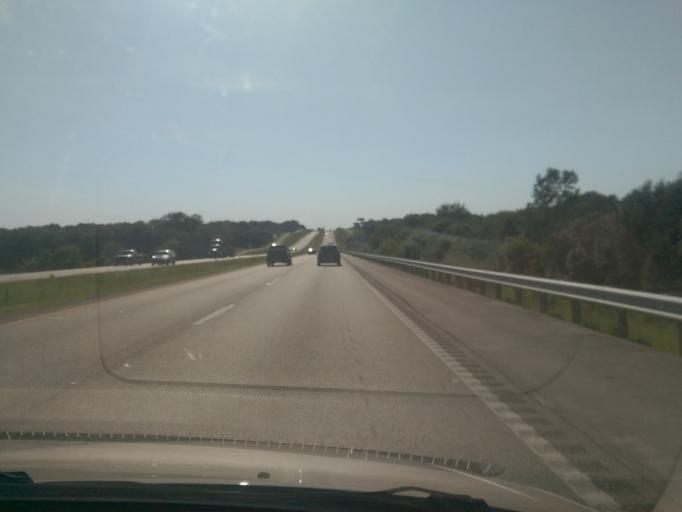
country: US
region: Missouri
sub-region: Saline County
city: Sweet Springs
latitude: 38.9744
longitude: -93.3591
